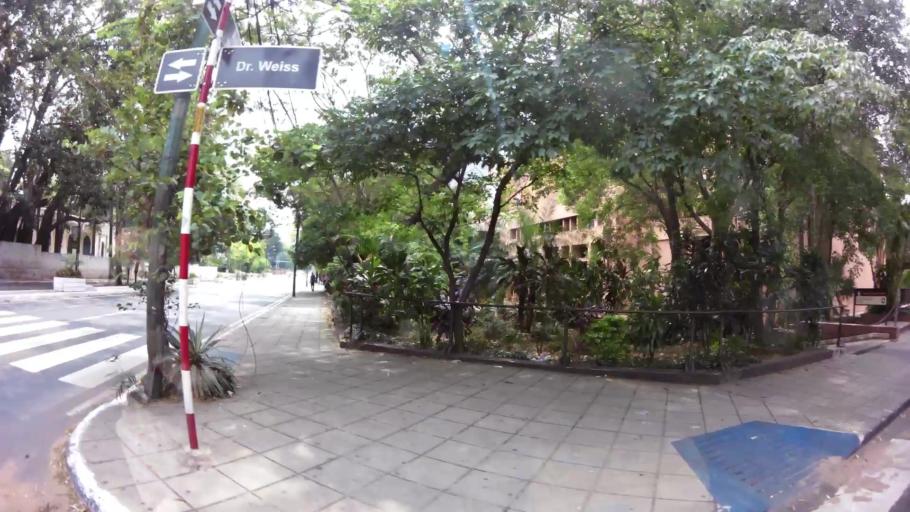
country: PY
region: Asuncion
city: Asuncion
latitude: -25.2929
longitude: -57.5825
